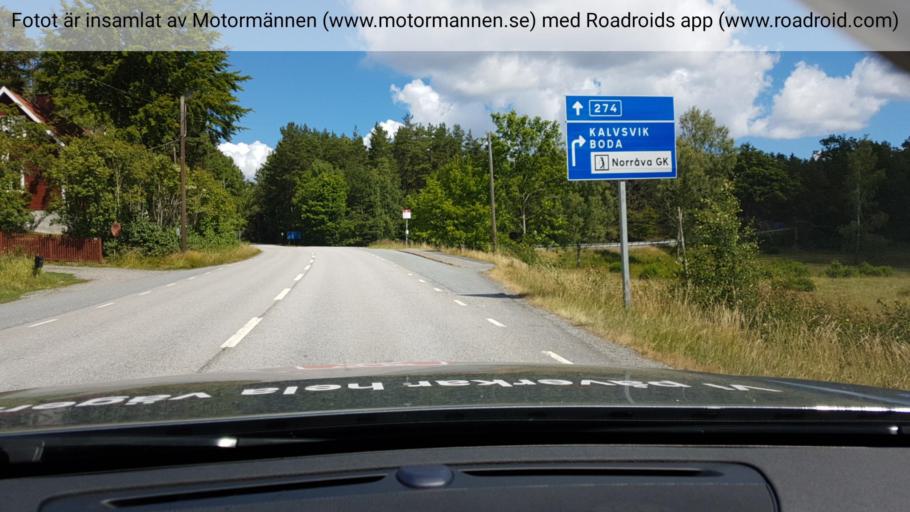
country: SE
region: Stockholm
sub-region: Varmdo Kommun
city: Hemmesta
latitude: 59.3620
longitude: 18.5171
